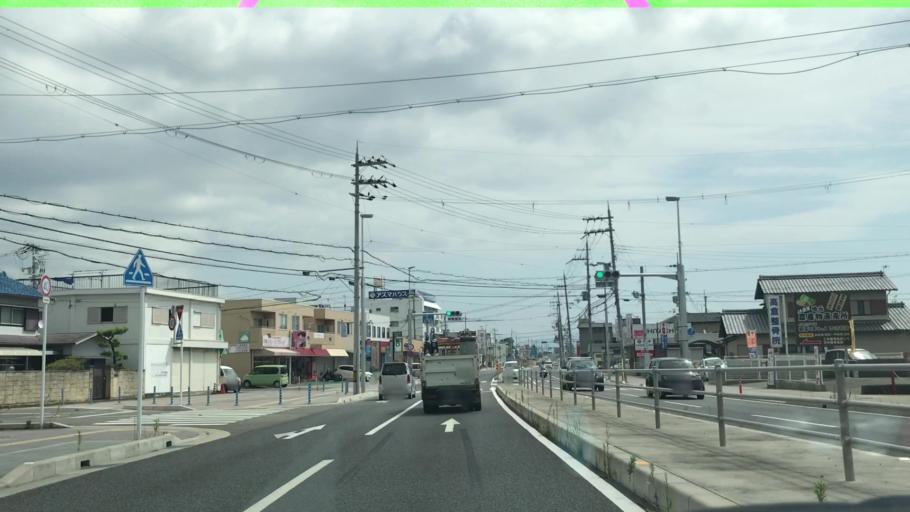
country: JP
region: Wakayama
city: Wakayama-shi
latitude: 34.2624
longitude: 135.1972
